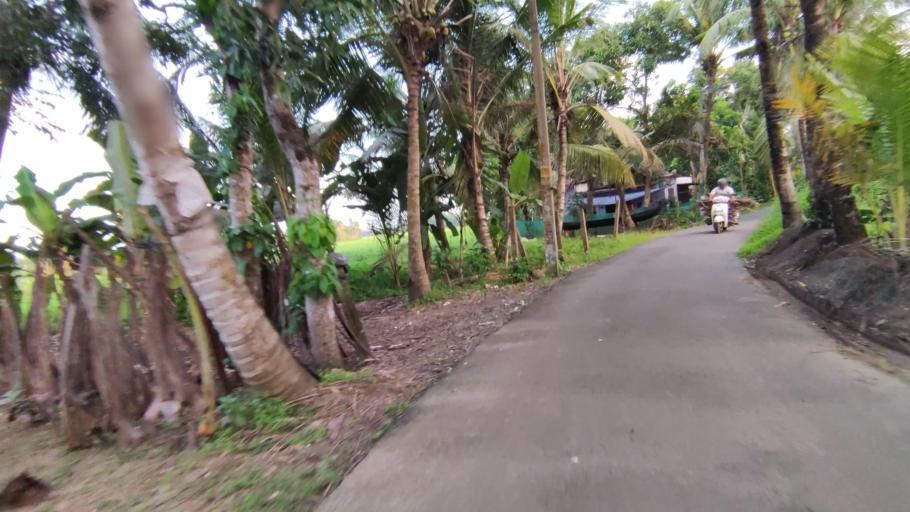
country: IN
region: Kerala
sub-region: Kottayam
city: Kottayam
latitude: 9.5832
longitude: 76.4482
